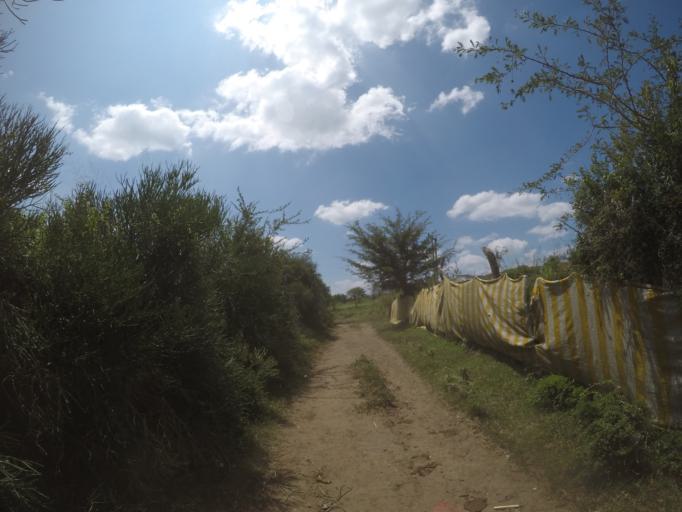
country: ZA
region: KwaZulu-Natal
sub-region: uThungulu District Municipality
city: Empangeni
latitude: -28.5969
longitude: 31.7364
